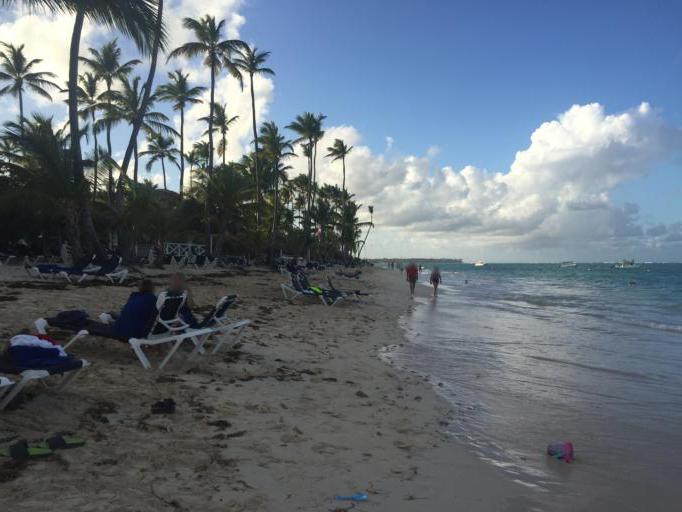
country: DO
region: San Juan
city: Punta Cana
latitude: 18.6941
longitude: -68.4253
